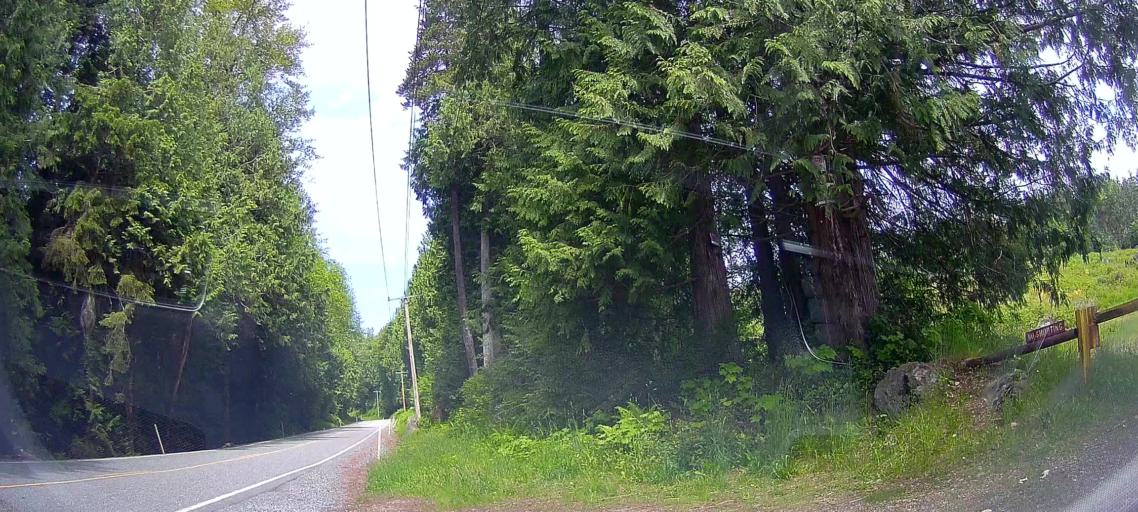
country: US
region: Washington
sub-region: Snohomish County
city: Bryant
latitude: 48.3347
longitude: -122.1679
